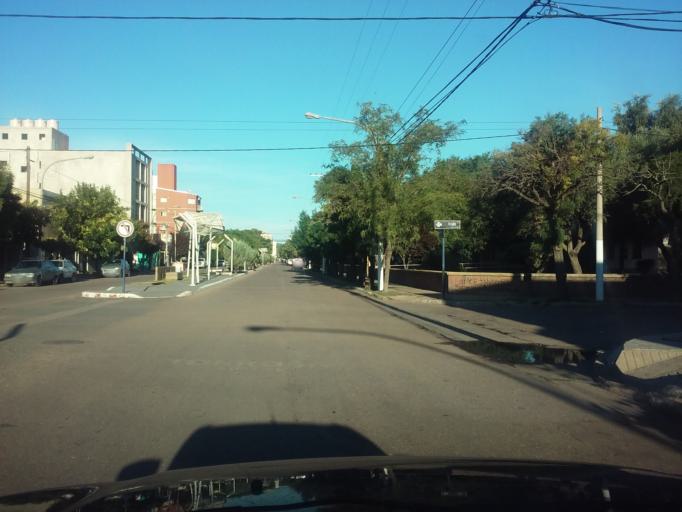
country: AR
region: La Pampa
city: Santa Rosa
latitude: -36.6210
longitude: -64.3005
